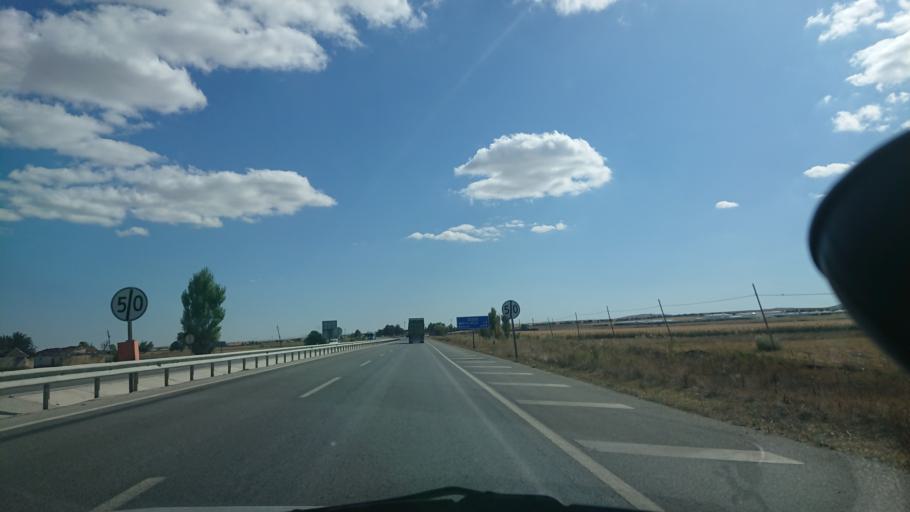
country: TR
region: Eskisehir
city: Mahmudiye
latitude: 39.5676
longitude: 30.9139
